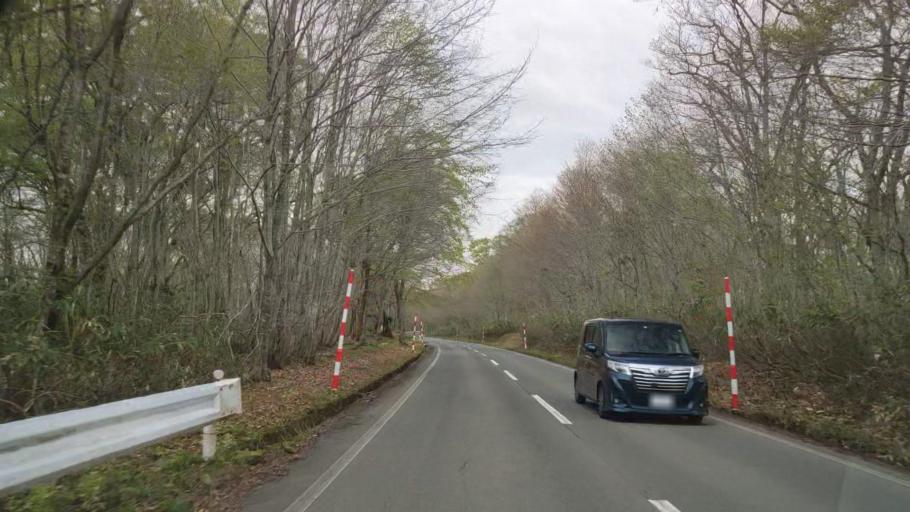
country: JP
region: Akita
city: Hanawa
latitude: 40.4044
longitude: 140.8084
